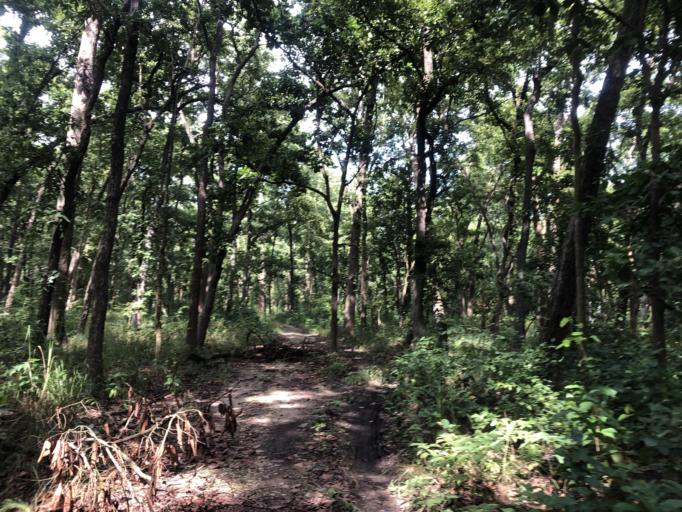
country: NP
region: Far Western
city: Tikapur
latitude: 28.5370
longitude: 81.2845
